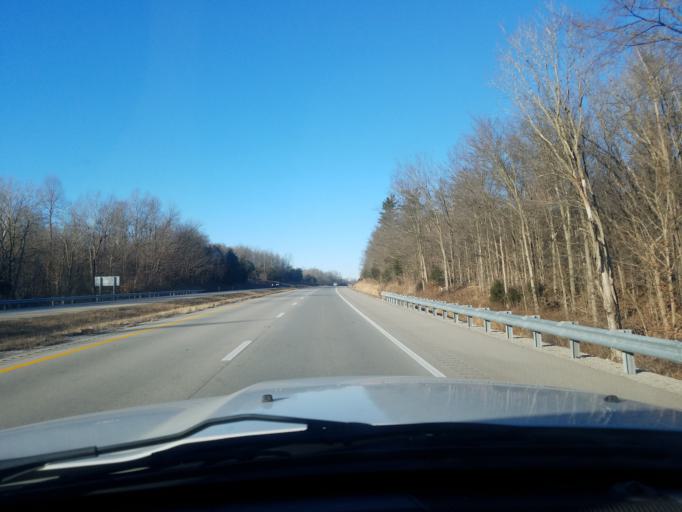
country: US
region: Kentucky
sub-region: Grayson County
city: Leitchfield
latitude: 37.4085
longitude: -86.4635
